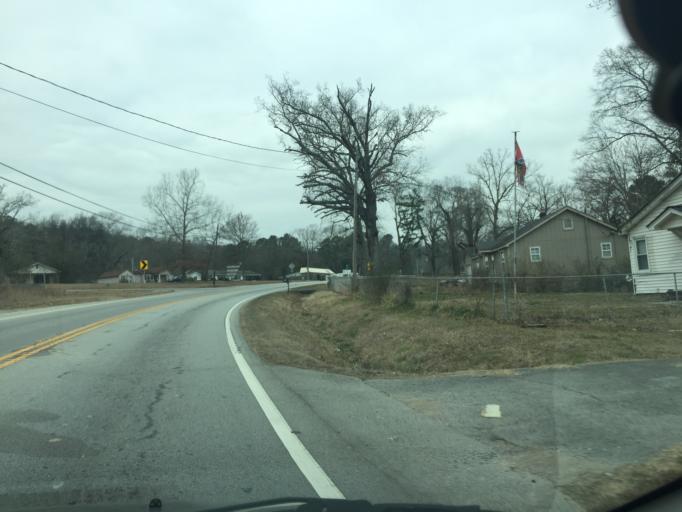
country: US
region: Georgia
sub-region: Catoosa County
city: Indian Springs
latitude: 34.9665
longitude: -85.1813
